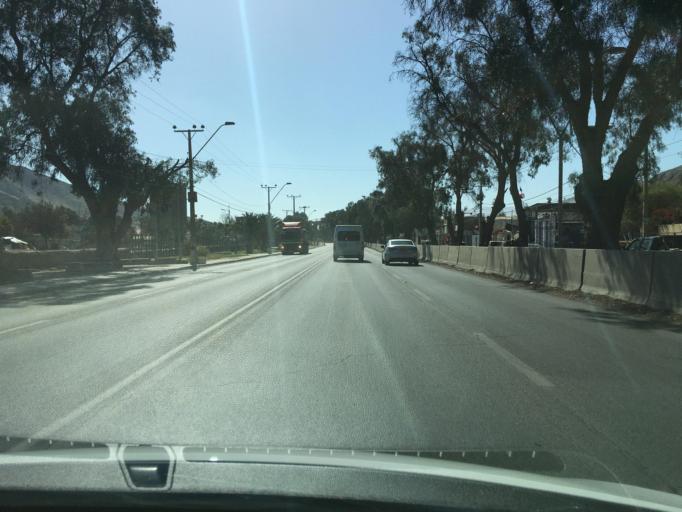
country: CL
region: Atacama
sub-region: Provincia de Copiapo
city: Copiapo
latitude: -27.3678
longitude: -70.3384
